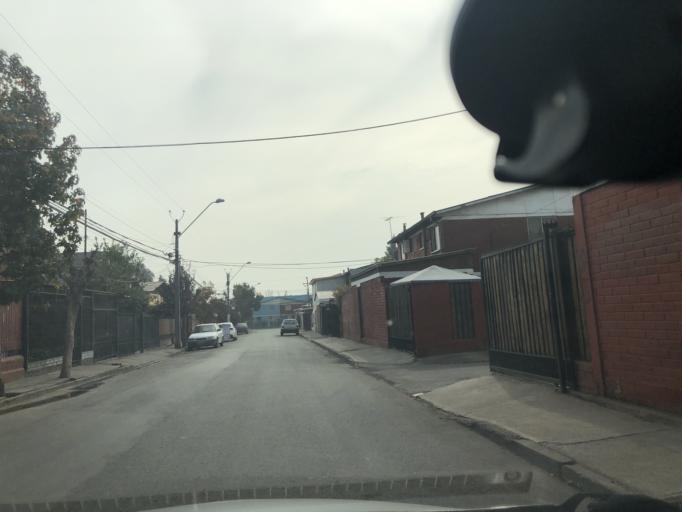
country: CL
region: Santiago Metropolitan
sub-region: Provincia de Cordillera
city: Puente Alto
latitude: -33.5635
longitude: -70.5654
